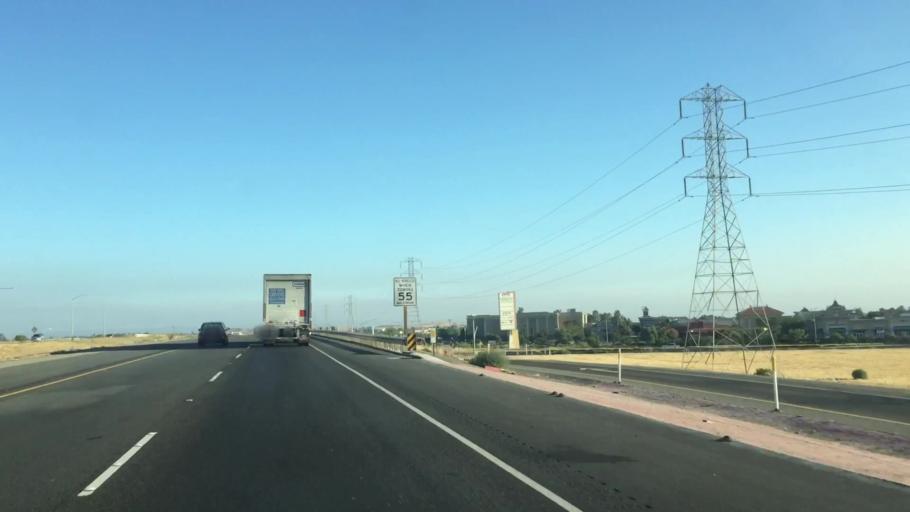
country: US
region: California
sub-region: Contra Costa County
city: Brentwood
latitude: 37.9414
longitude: -121.7403
